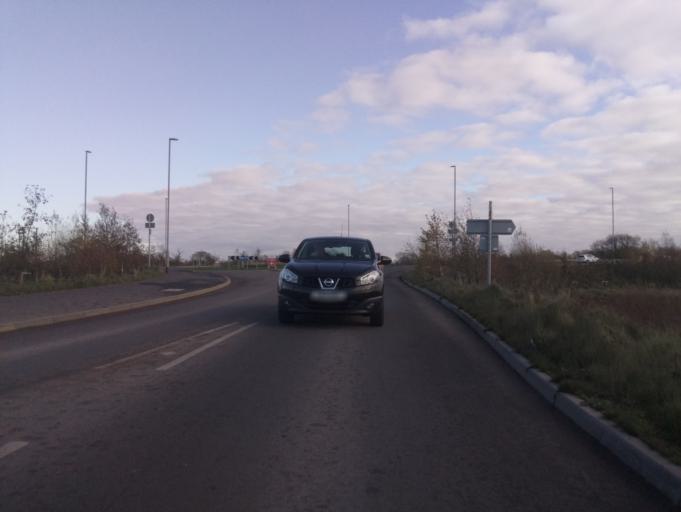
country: GB
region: England
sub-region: Staffordshire
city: Burton upon Trent
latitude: 52.7903
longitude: -1.6811
